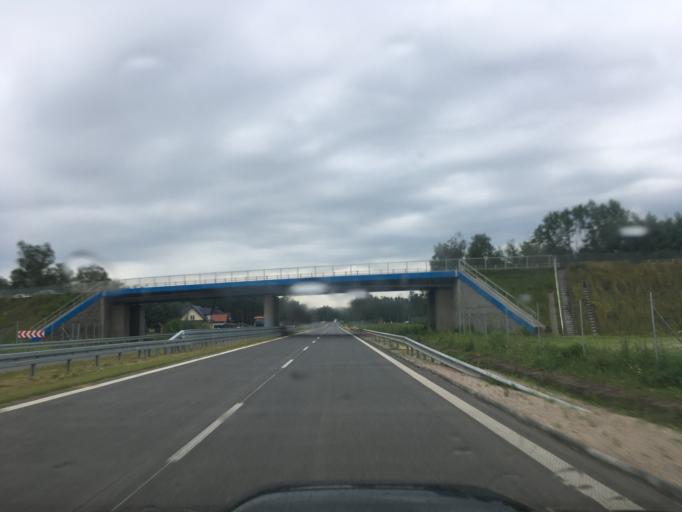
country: PL
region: Masovian Voivodeship
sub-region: Powiat piaseczynski
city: Gora Kalwaria
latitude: 51.9782
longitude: 21.1845
